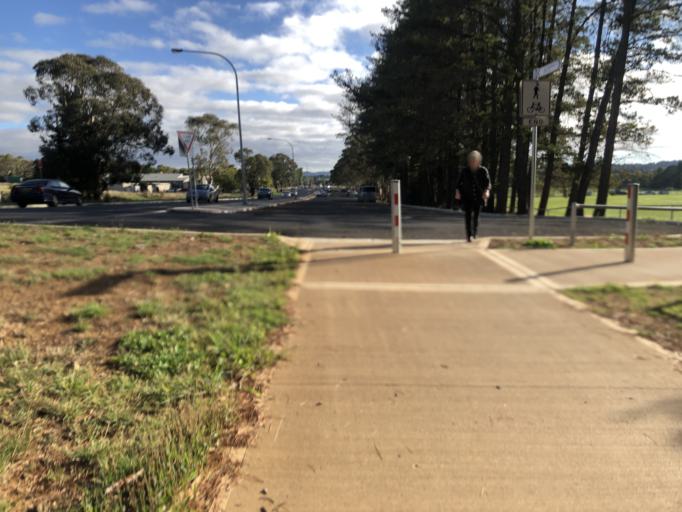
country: AU
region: New South Wales
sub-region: Orange Municipality
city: Orange
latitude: -33.3099
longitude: 149.0964
